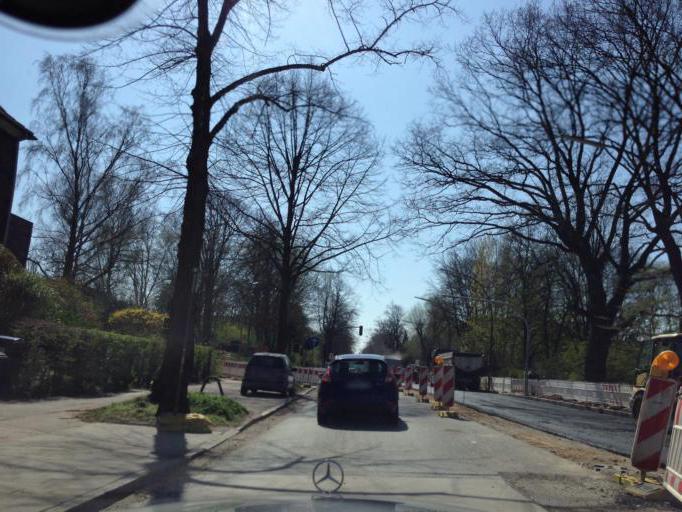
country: DE
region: Hamburg
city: Fuhlsbuettel
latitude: 53.6279
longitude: 10.0133
